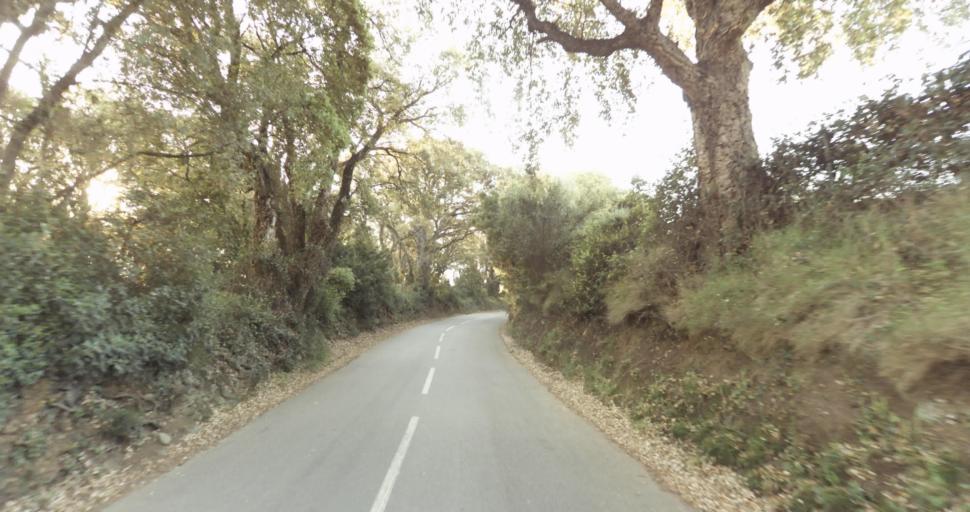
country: FR
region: Corsica
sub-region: Departement de la Haute-Corse
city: Biguglia
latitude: 42.6241
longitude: 9.4430
